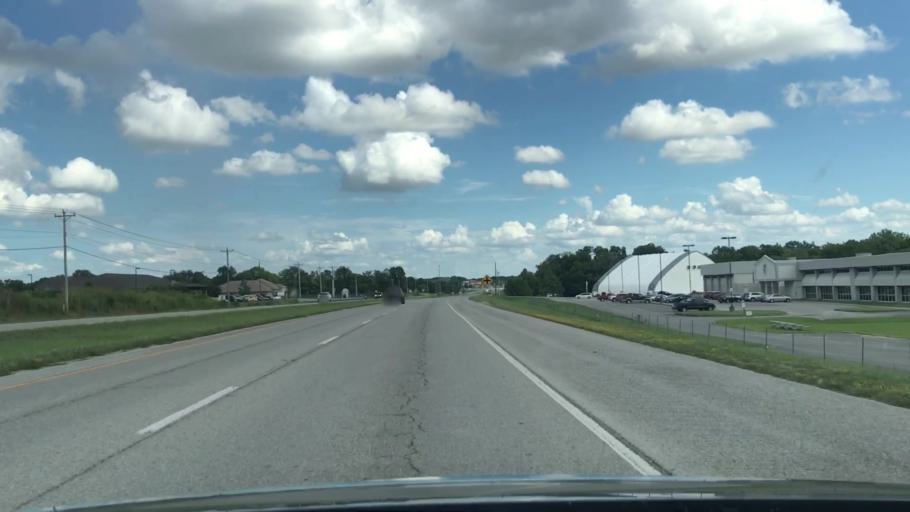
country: US
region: Kentucky
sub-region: Christian County
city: Hopkinsville
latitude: 36.8307
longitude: -87.5209
